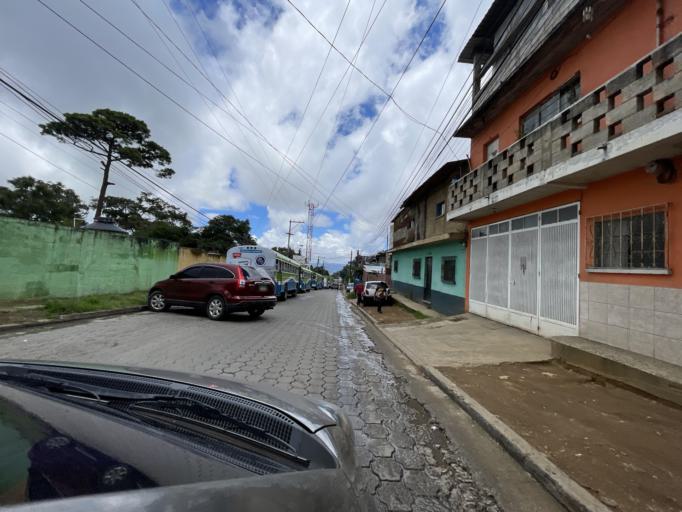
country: GT
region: Guatemala
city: Mixco
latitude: 14.6373
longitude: -90.6201
